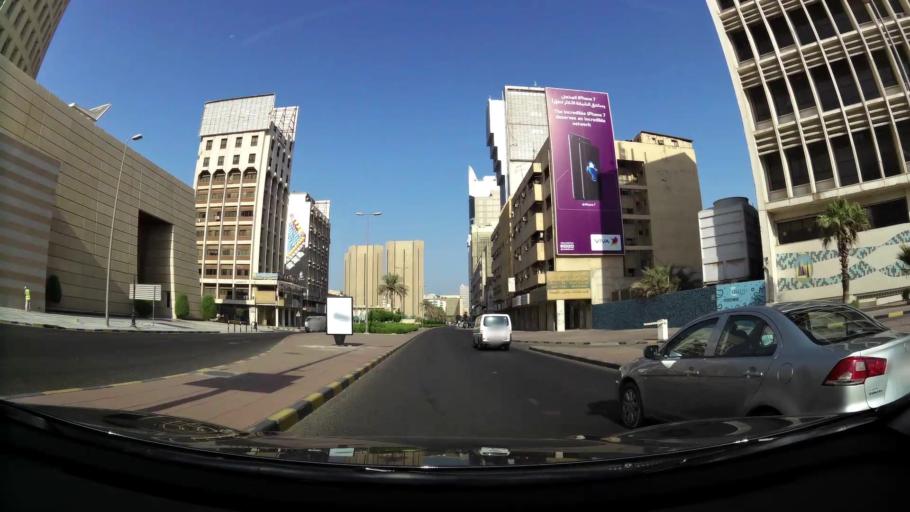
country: KW
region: Al Asimah
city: Kuwait City
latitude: 29.3725
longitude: 47.9821
